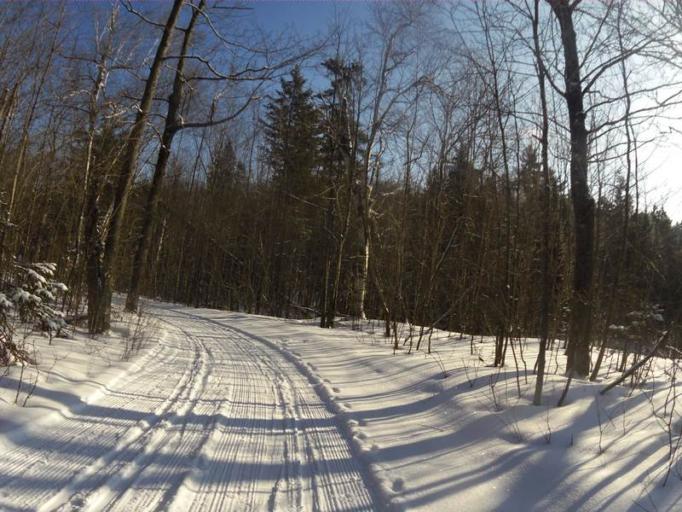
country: CA
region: Quebec
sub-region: Outaouais
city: Wakefield
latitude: 45.5273
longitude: -75.9220
